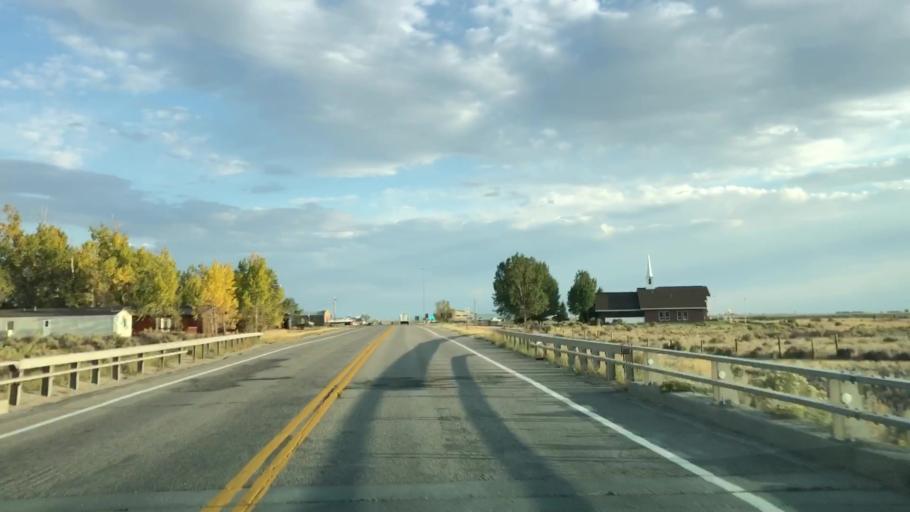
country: US
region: Wyoming
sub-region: Sweetwater County
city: North Rock Springs
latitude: 42.1133
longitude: -109.4506
